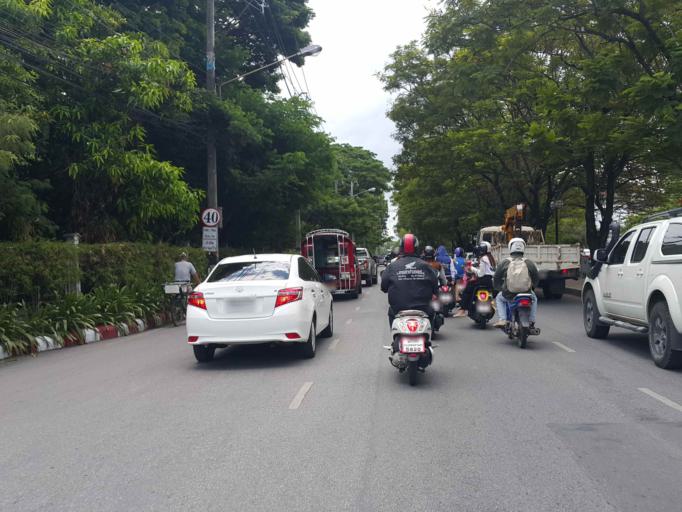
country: TH
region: Chiang Mai
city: Chiang Mai
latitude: 18.7904
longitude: 98.9779
